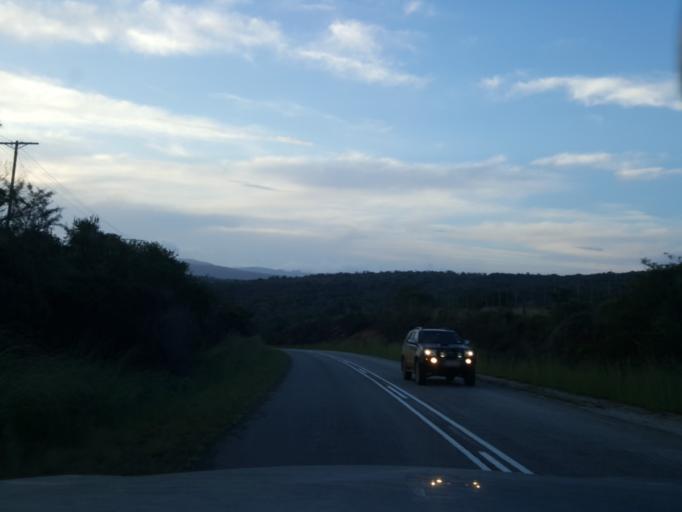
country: ZA
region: Eastern Cape
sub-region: Cacadu District Municipality
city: Grahamstown
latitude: -33.4079
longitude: 26.4771
